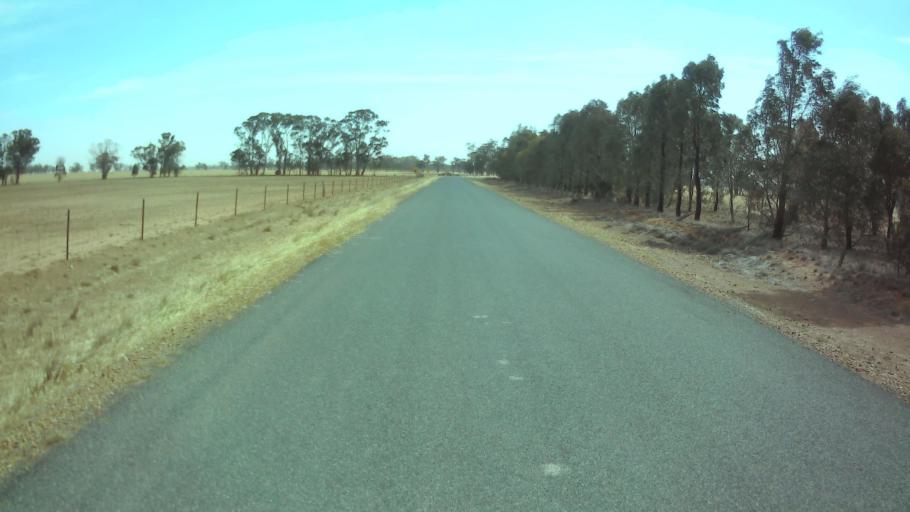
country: AU
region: New South Wales
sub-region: Weddin
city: Grenfell
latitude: -33.7109
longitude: 148.0018
